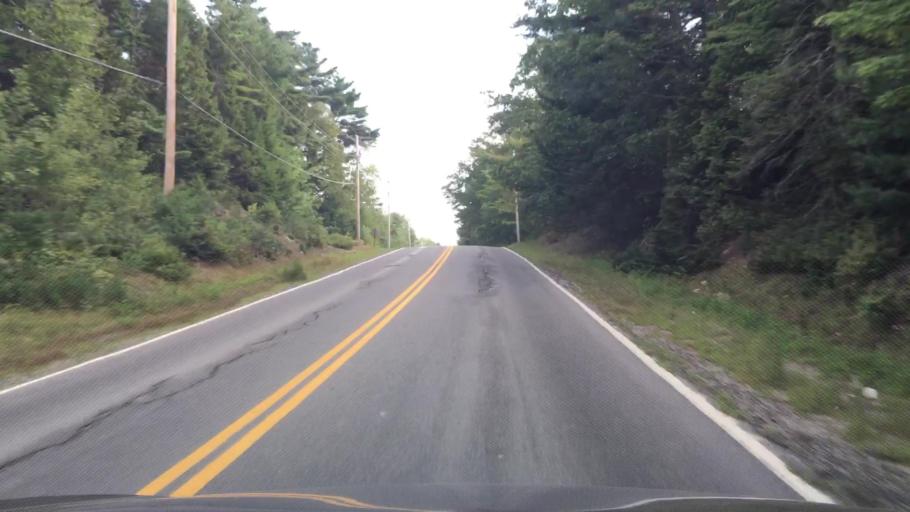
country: US
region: Maine
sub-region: Hancock County
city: Surry
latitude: 44.4389
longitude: -68.5705
